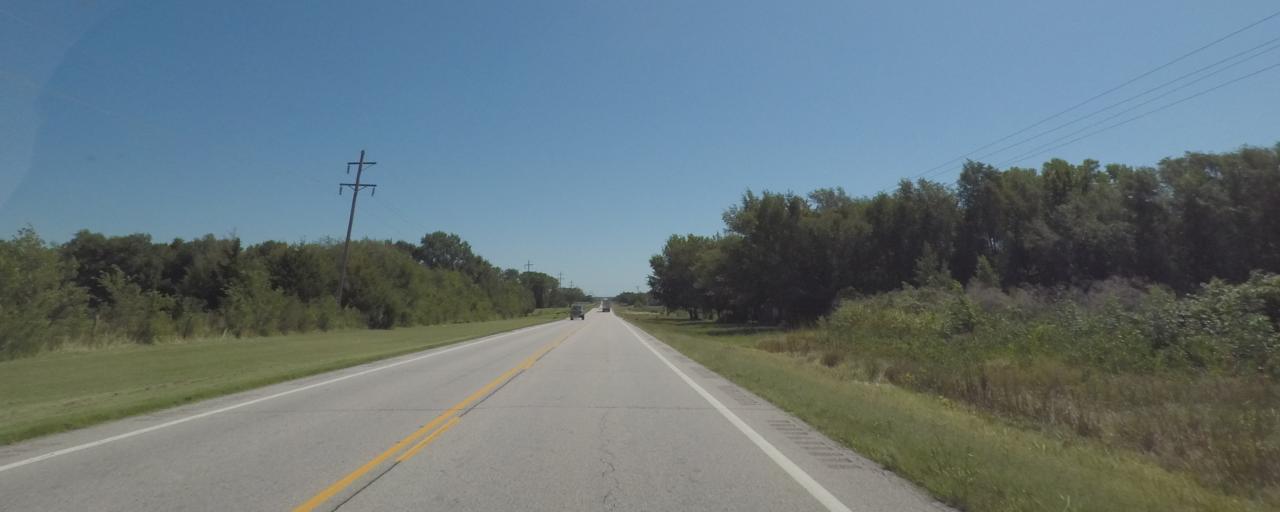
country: US
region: Kansas
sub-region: Sumner County
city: Belle Plaine
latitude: 37.3912
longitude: -97.3735
